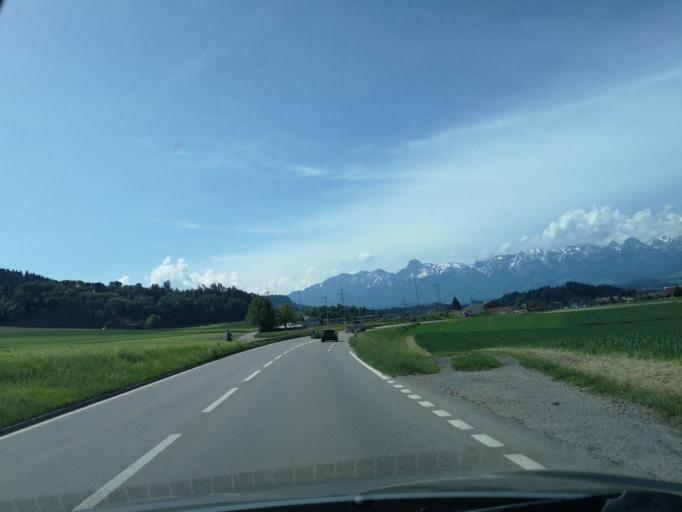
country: CH
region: Lucerne
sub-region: Entlebuch District
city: Oberdiessbach
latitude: 46.8354
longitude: 7.6178
